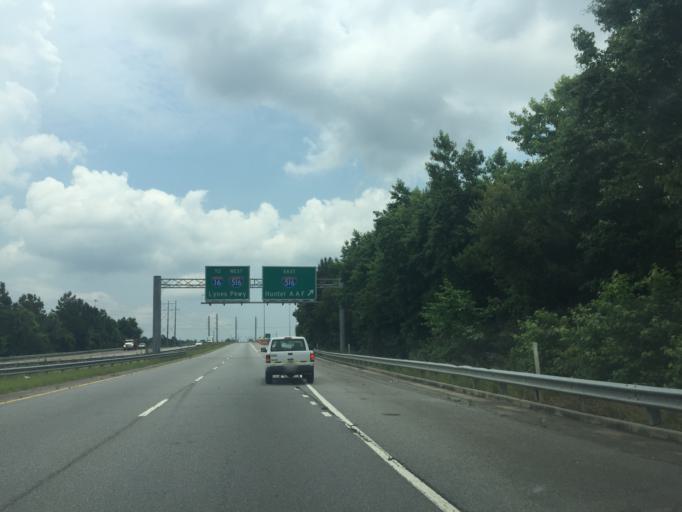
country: US
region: Georgia
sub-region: Chatham County
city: Savannah
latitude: 32.0420
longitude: -81.1520
